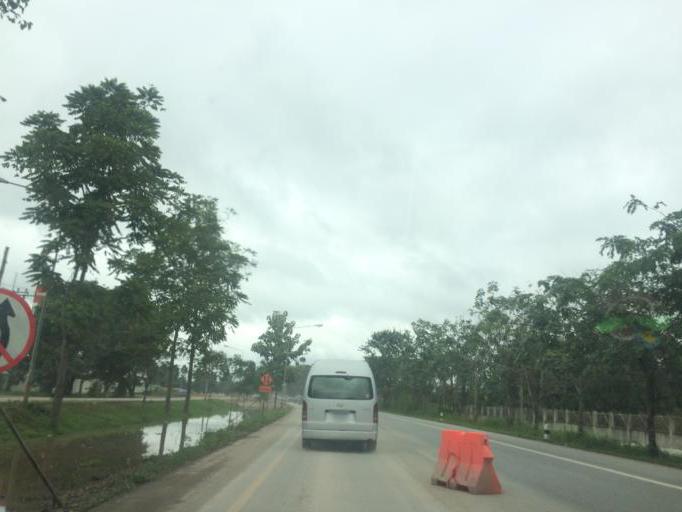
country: TH
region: Chiang Rai
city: Chiang Rai
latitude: 19.8419
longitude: 99.7979
